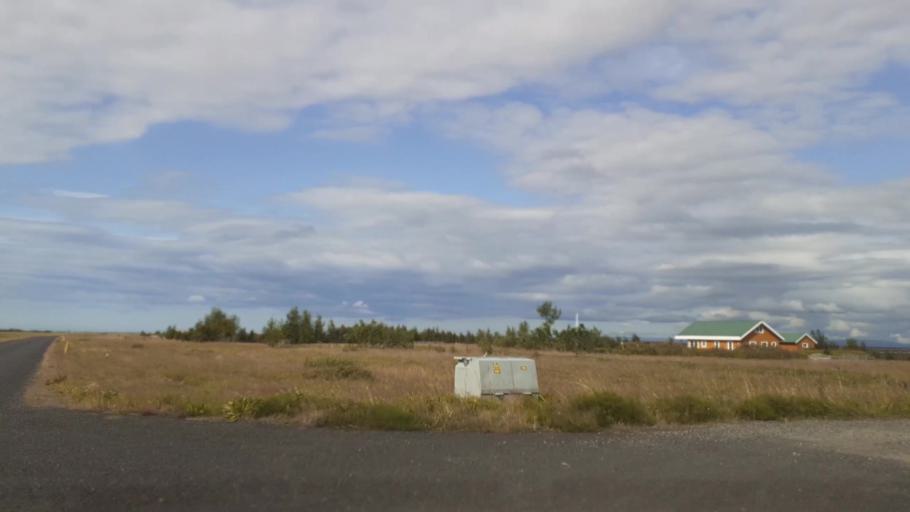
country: IS
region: South
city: Vestmannaeyjar
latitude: 63.7693
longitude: -20.2963
